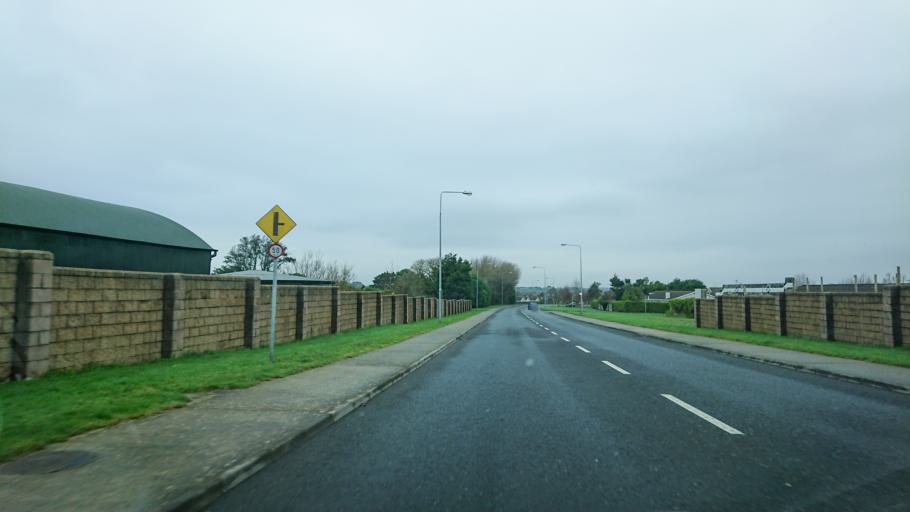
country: IE
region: Munster
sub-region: Waterford
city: Tra Mhor
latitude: 52.1569
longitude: -7.1696
